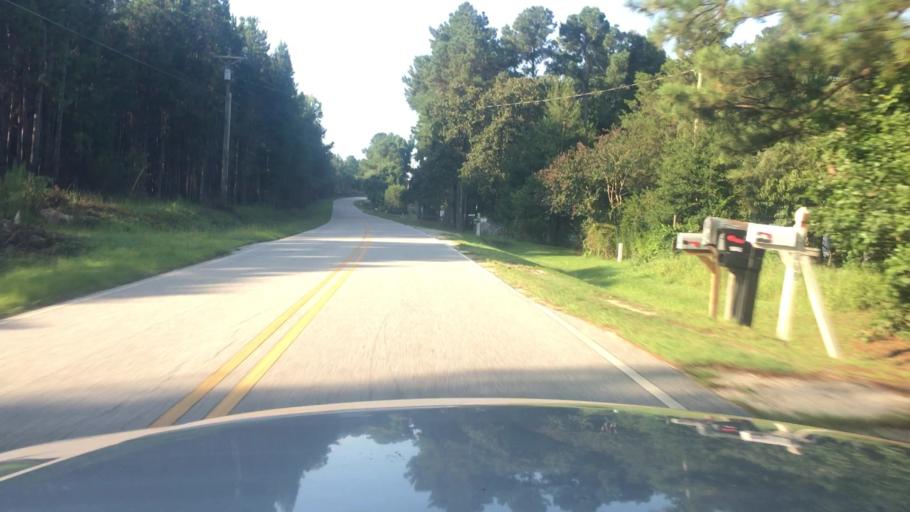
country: US
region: North Carolina
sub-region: Cumberland County
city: Spring Lake
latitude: 35.2197
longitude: -78.8935
